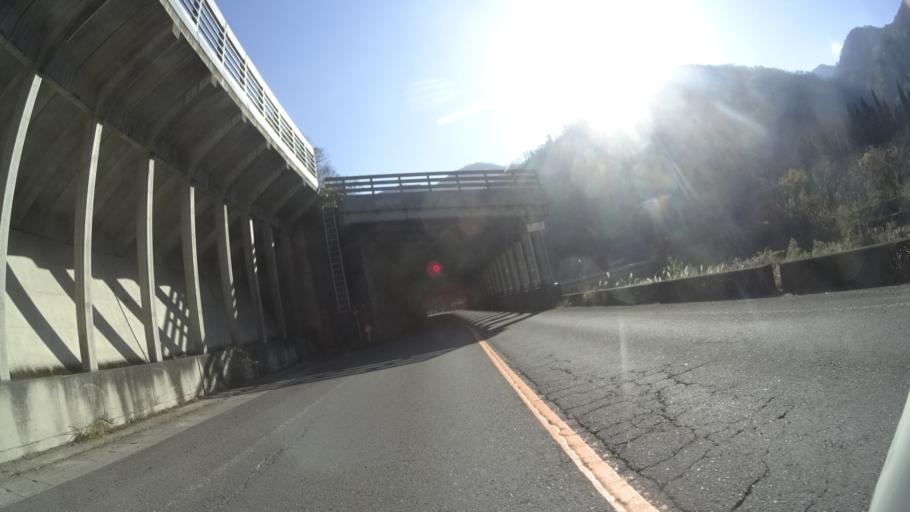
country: JP
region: Fukui
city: Ono
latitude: 35.9184
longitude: 136.6257
